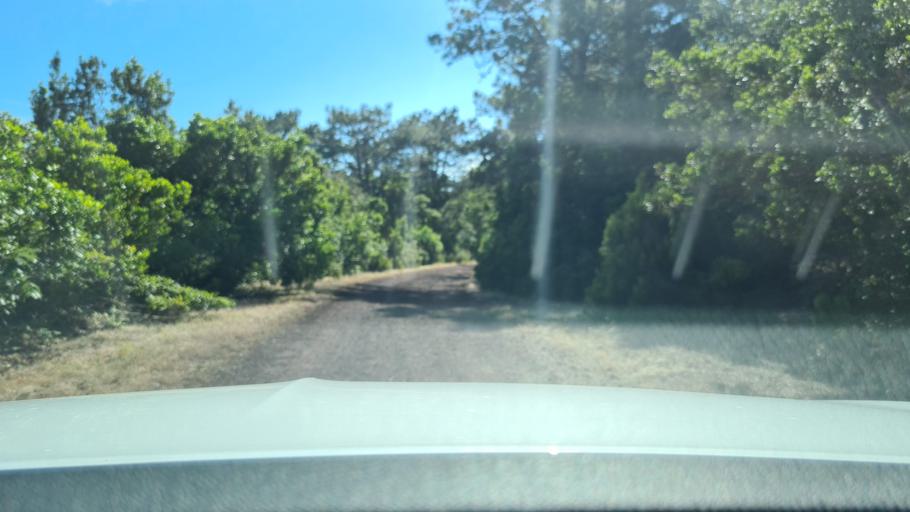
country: PT
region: Azores
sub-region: Sao Roque do Pico
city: Sao Roque do Pico
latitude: 38.4126
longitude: -28.3140
